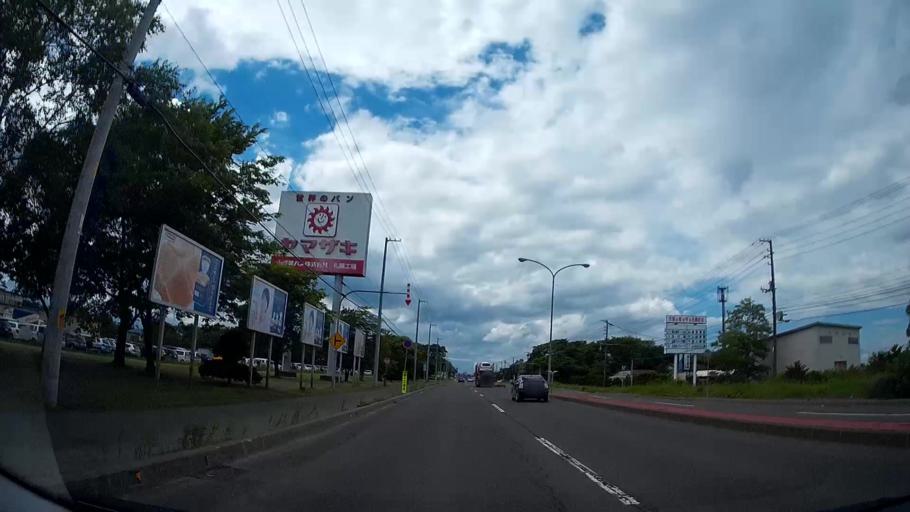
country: JP
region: Hokkaido
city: Chitose
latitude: 42.8663
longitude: 141.5935
